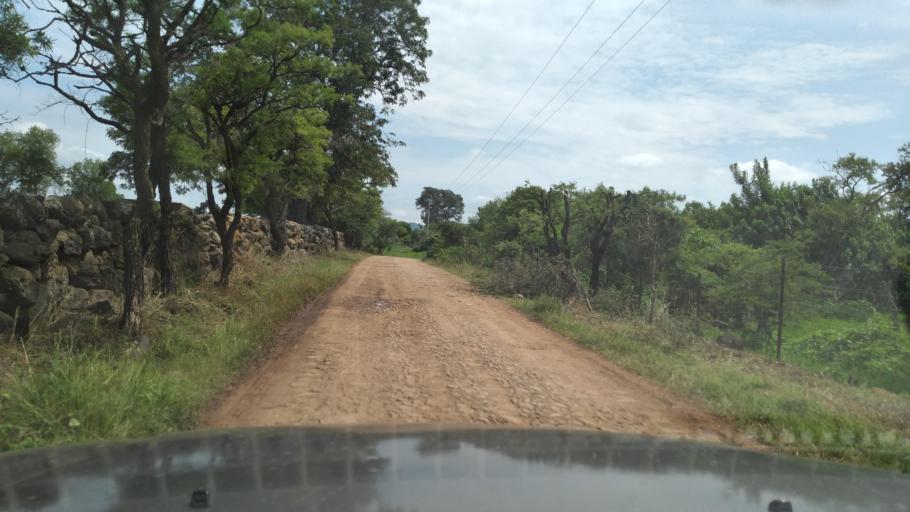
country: MX
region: Jalisco
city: Capilla de Guadalupe
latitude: 20.7464
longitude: -102.6325
